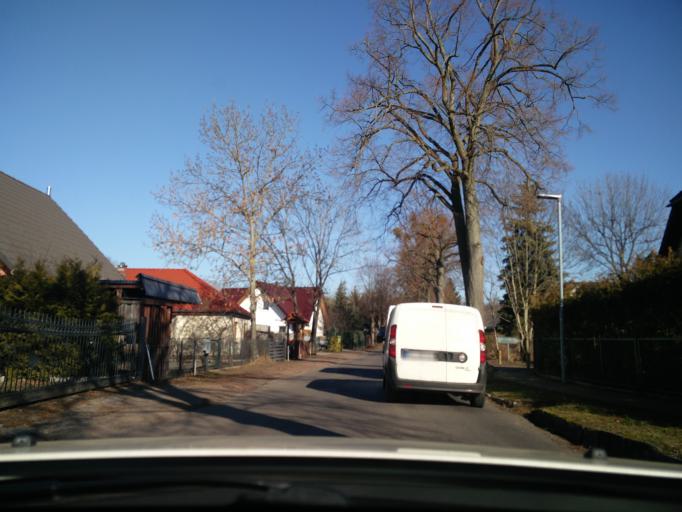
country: DE
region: Brandenburg
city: Brieselang
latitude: 52.5778
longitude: 12.9965
